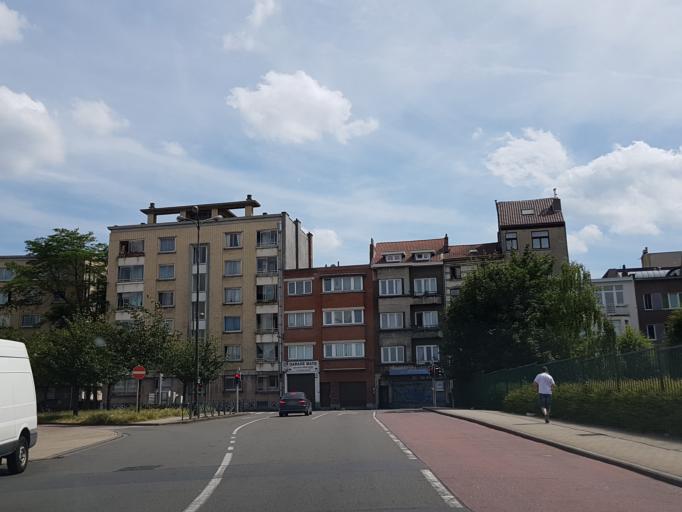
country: BE
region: Brussels Capital
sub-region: Bruxelles-Capitale
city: Brussels
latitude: 50.8705
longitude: 4.3891
